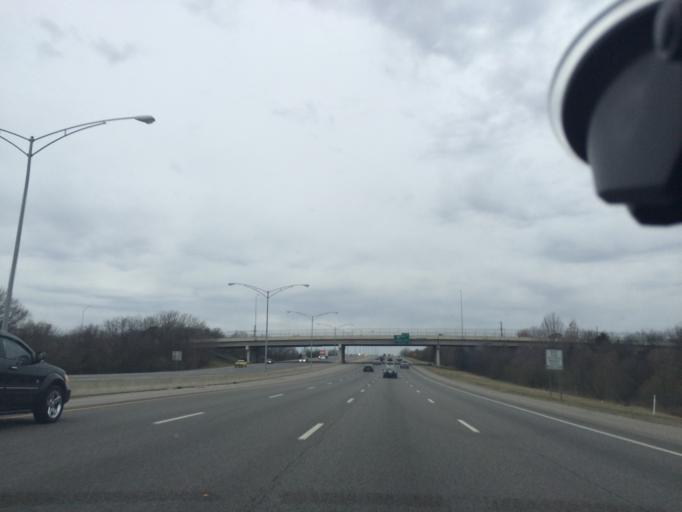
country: US
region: Alabama
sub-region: Madison County
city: Huntsville
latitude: 34.7255
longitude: -86.6072
